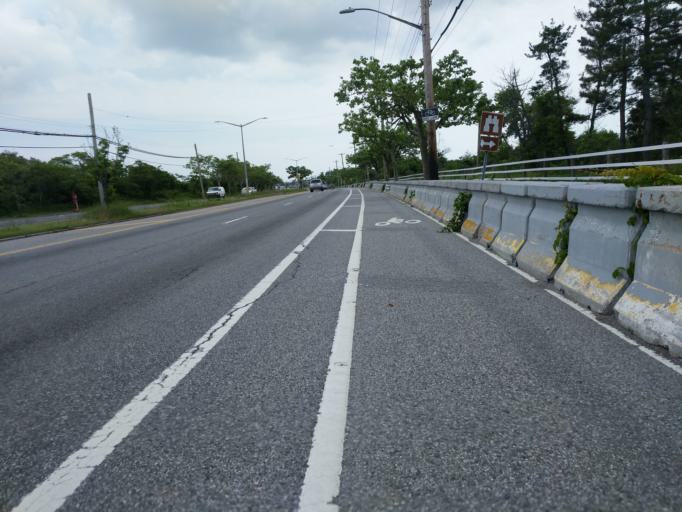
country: US
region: New York
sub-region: Queens County
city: Borough of Queens
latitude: 40.6191
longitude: -73.8251
